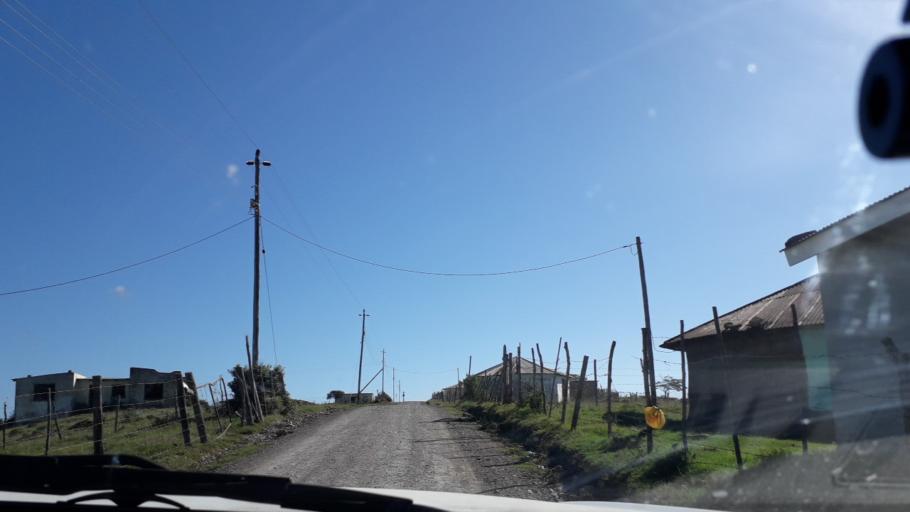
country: ZA
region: Eastern Cape
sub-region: Buffalo City Metropolitan Municipality
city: East London
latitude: -32.7995
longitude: 27.9601
